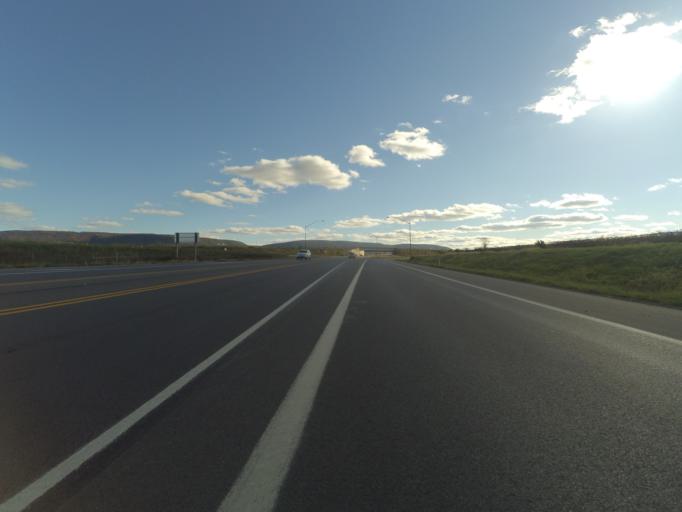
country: US
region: Pennsylvania
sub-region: Centre County
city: Pleasant Gap
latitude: 40.8764
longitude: -77.7785
